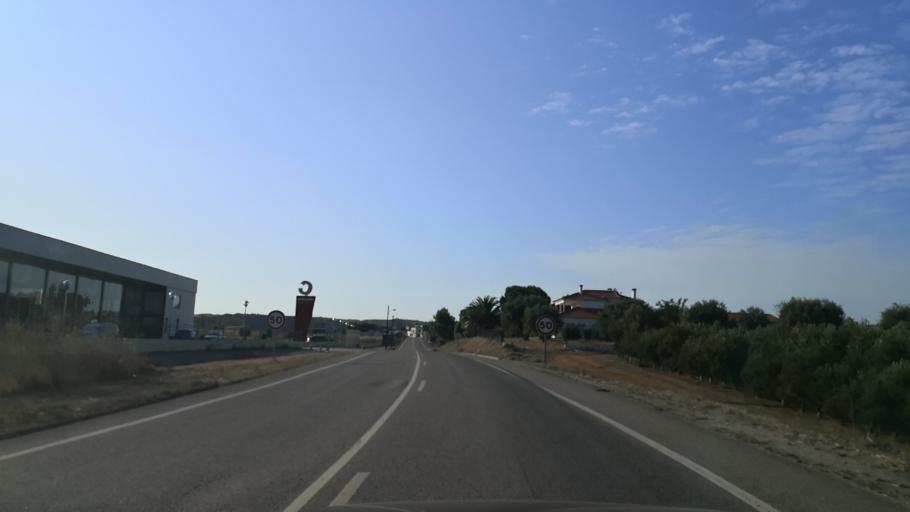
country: PT
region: Santarem
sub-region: Santarem
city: Santarem
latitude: 39.3326
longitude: -8.6591
